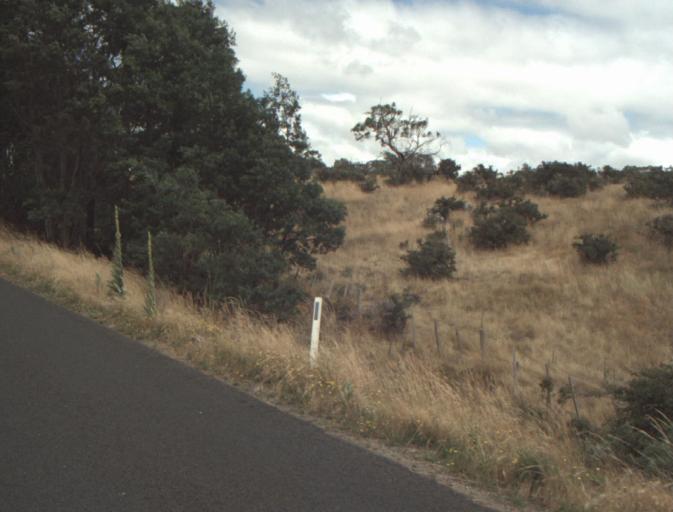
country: AU
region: Tasmania
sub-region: Northern Midlands
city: Evandale
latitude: -41.5073
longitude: 147.3657
